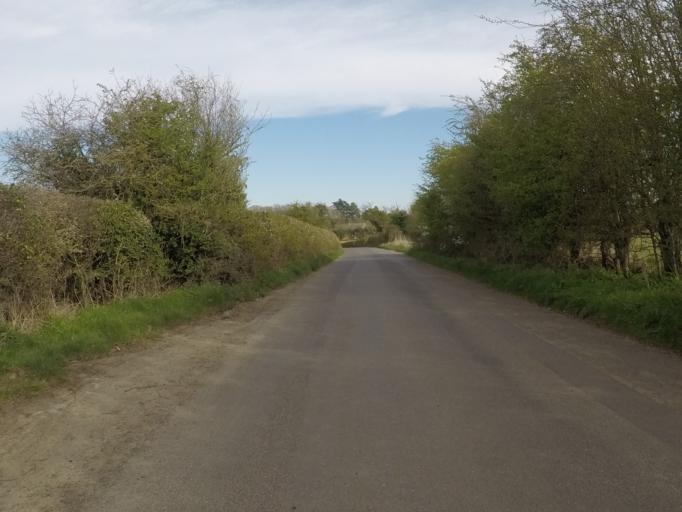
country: GB
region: England
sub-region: Oxfordshire
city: Charlbury
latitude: 51.8426
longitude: -1.4711
